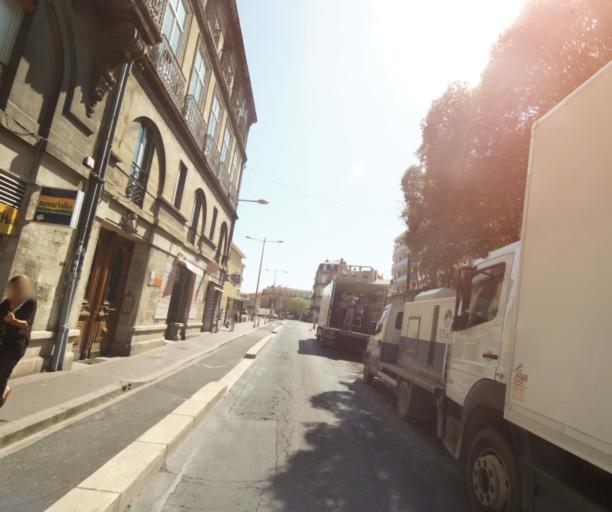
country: FR
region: Languedoc-Roussillon
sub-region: Departement de l'Herault
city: Montpellier
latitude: 43.6047
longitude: 3.8751
